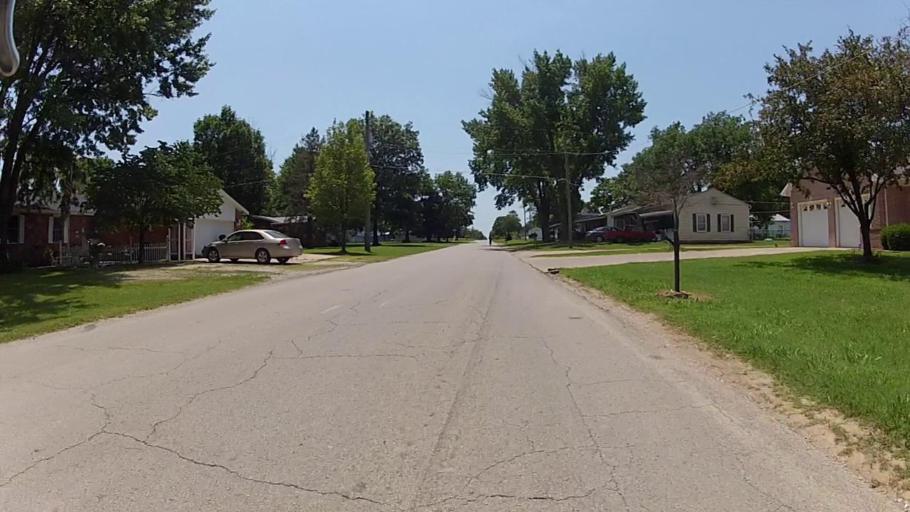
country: US
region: Kansas
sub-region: Montgomery County
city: Cherryvale
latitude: 37.2662
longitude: -95.5370
